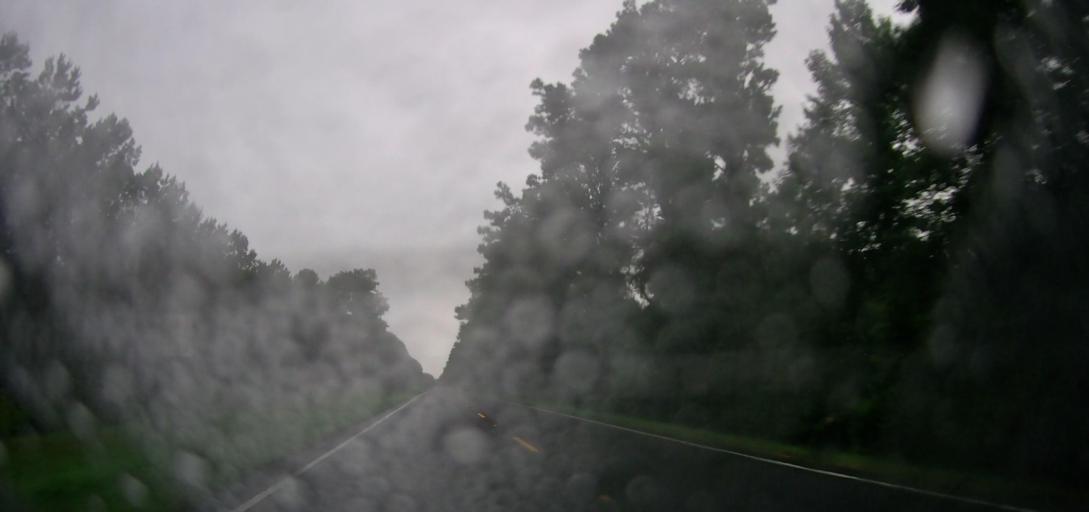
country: US
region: Georgia
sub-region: Glynn County
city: Dock Junction
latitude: 31.2730
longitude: -81.6483
